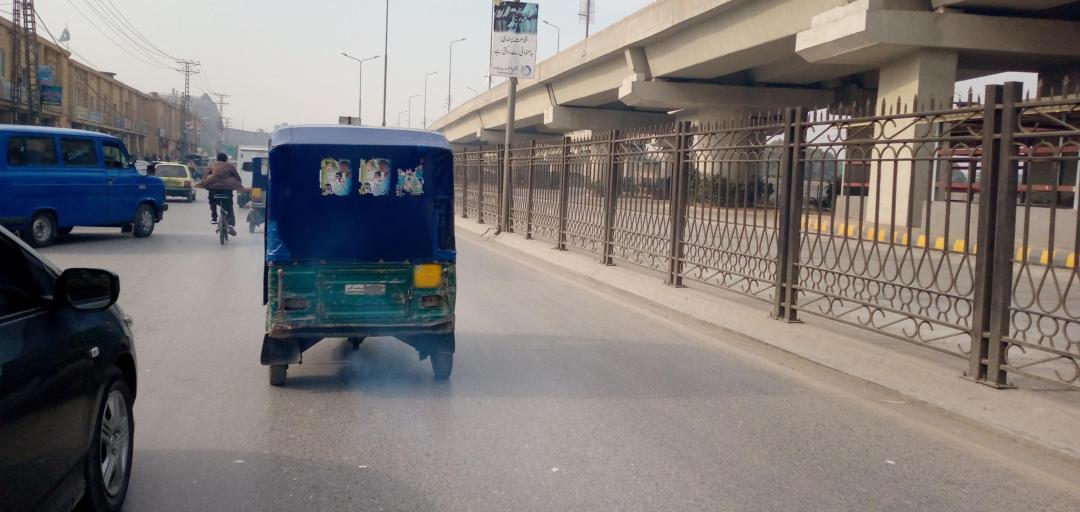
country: PK
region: Khyber Pakhtunkhwa
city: Peshawar
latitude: 34.0145
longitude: 71.5732
